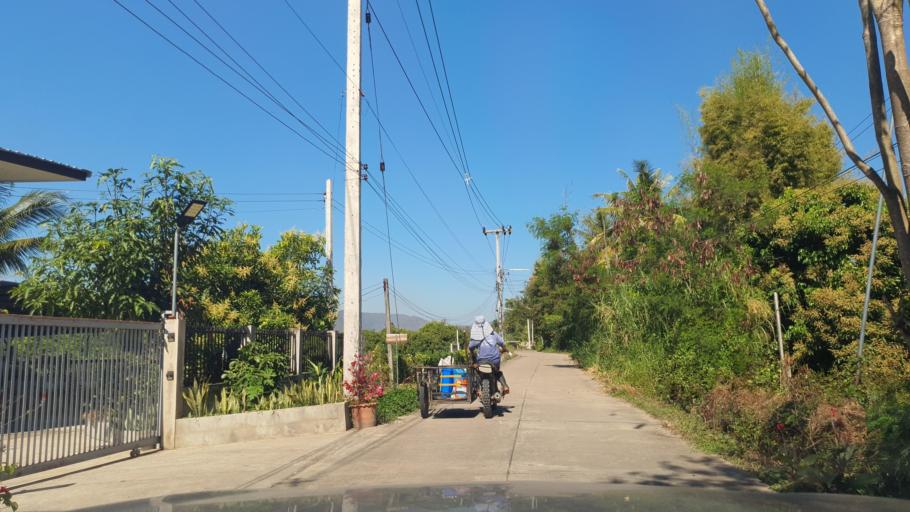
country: TH
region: Chiang Mai
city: Mae Wang
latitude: 18.6611
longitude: 98.8295
